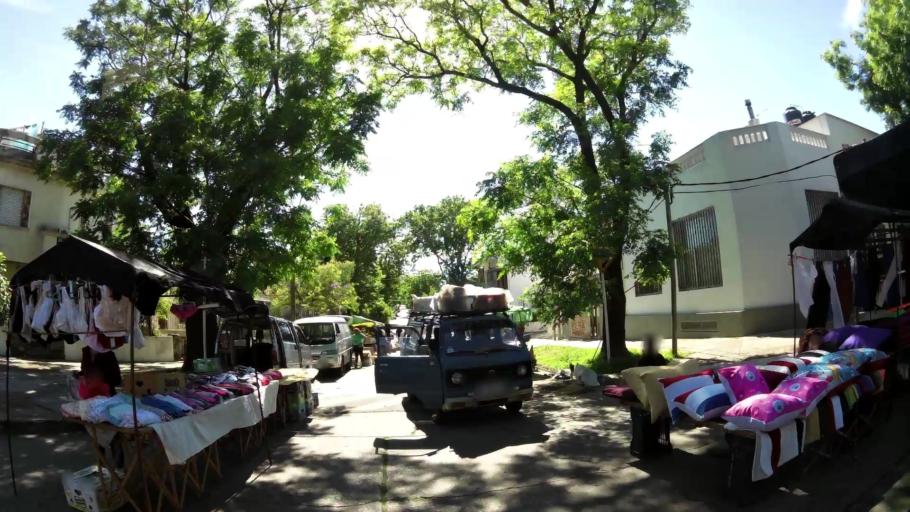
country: UY
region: Montevideo
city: Montevideo
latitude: -34.9007
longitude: -56.1512
